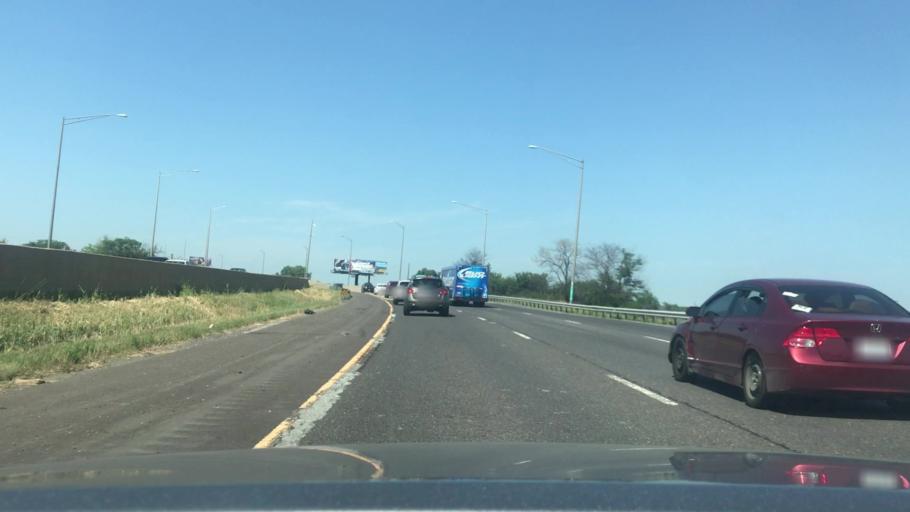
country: US
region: Illinois
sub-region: Cook County
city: Dixmoor
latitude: 41.6371
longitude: -87.6621
